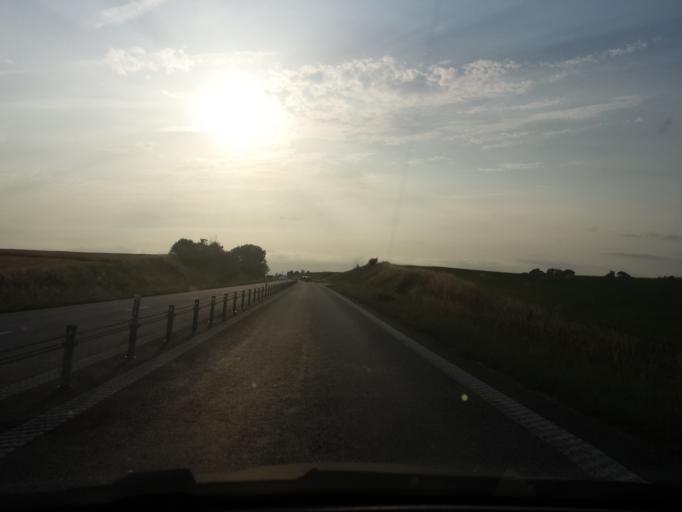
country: SE
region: Skane
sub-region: Skurups Kommun
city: Rydsgard
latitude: 55.4804
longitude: 13.6203
